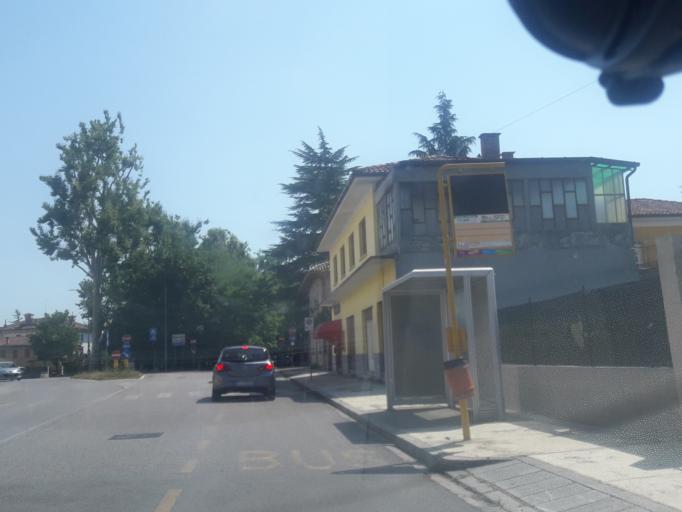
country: IT
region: Friuli Venezia Giulia
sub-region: Provincia di Udine
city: Udine
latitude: 46.0832
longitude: 13.2371
